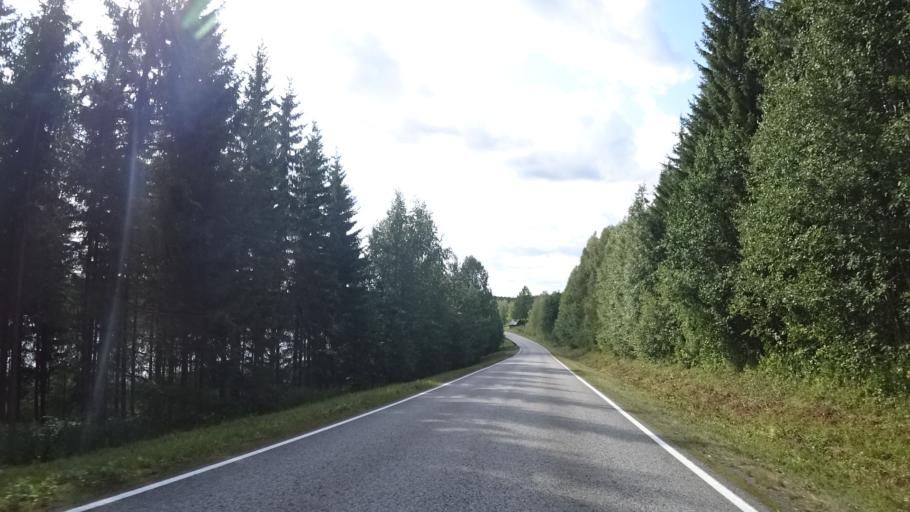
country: RU
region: Republic of Karelia
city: Vyartsilya
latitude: 62.2693
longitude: 30.7920
